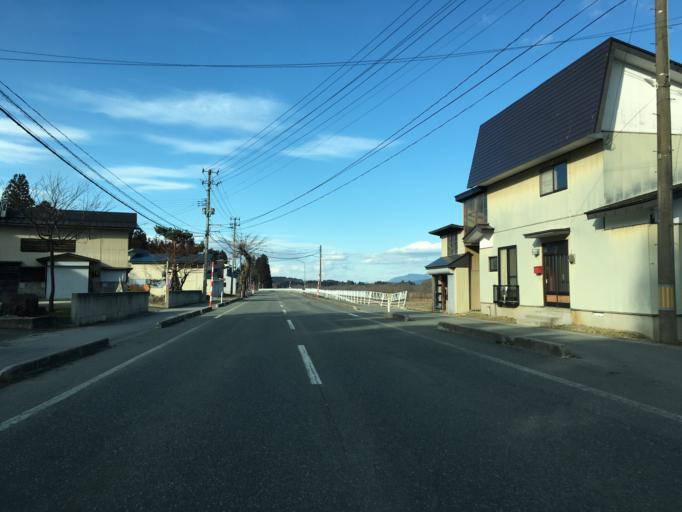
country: JP
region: Yamagata
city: Nagai
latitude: 37.9988
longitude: 139.9581
